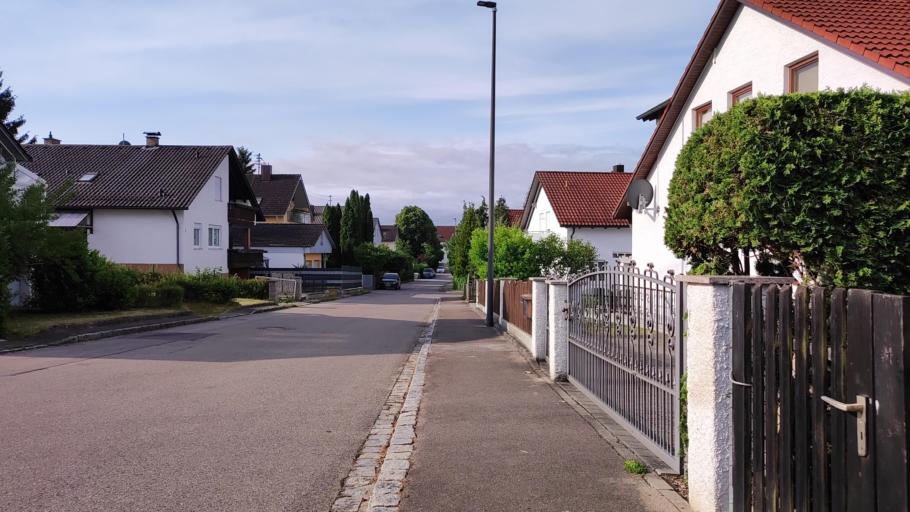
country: DE
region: Bavaria
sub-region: Swabia
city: Horgau
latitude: 48.3985
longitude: 10.6957
